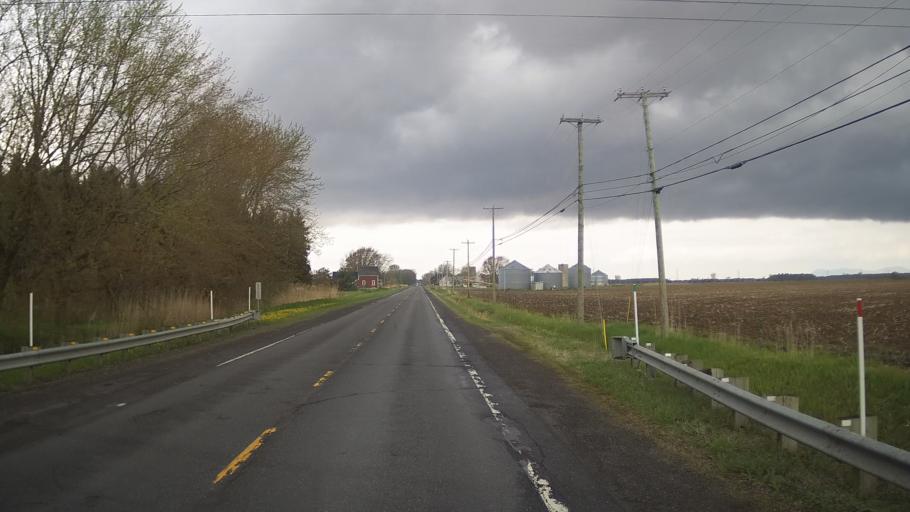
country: CA
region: Quebec
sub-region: Monteregie
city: Rougemont
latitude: 45.3325
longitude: -73.0784
